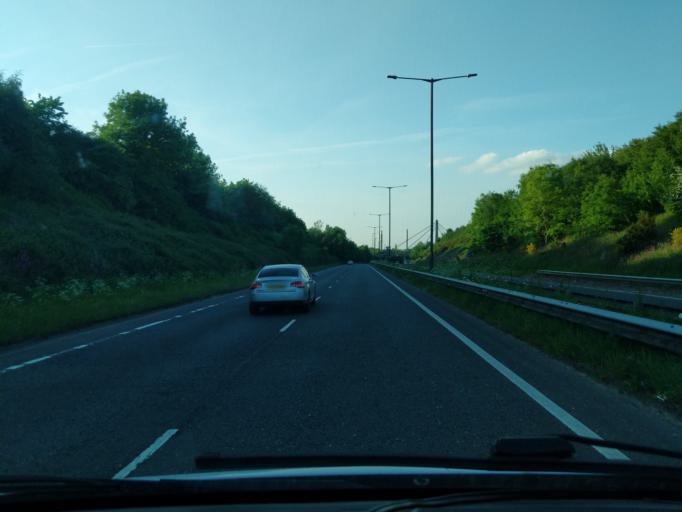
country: GB
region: England
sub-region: St. Helens
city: St Helens
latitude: 53.4306
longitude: -2.7402
